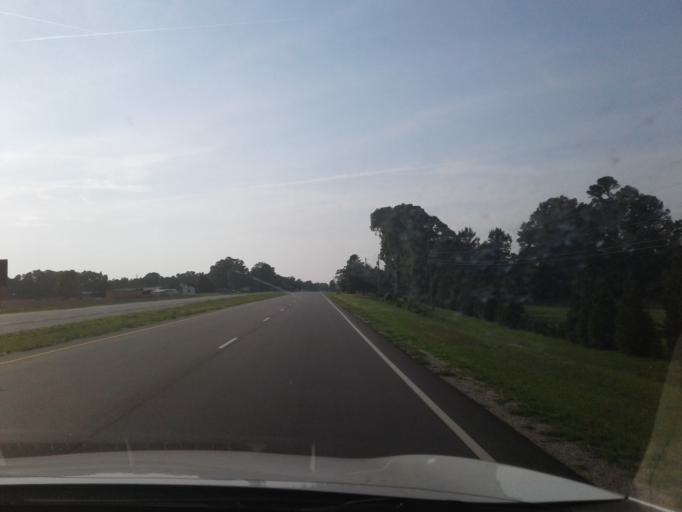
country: US
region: North Carolina
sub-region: Harnett County
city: Erwin
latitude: 35.3528
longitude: -78.6935
